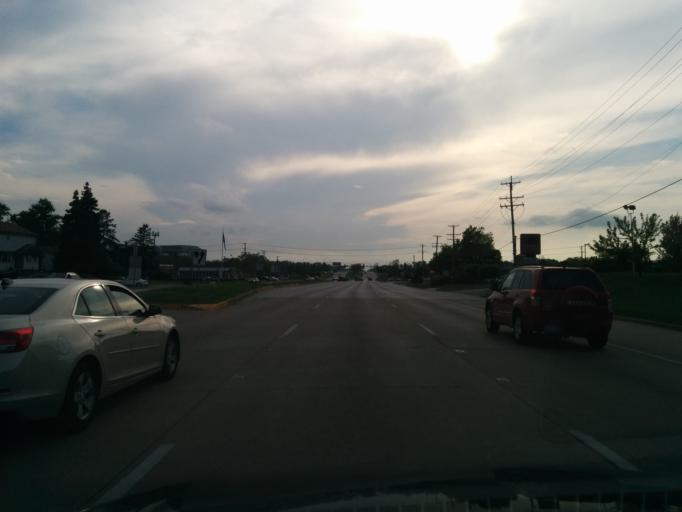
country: US
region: Illinois
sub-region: DuPage County
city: Lombard
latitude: 41.9045
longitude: -88.0297
